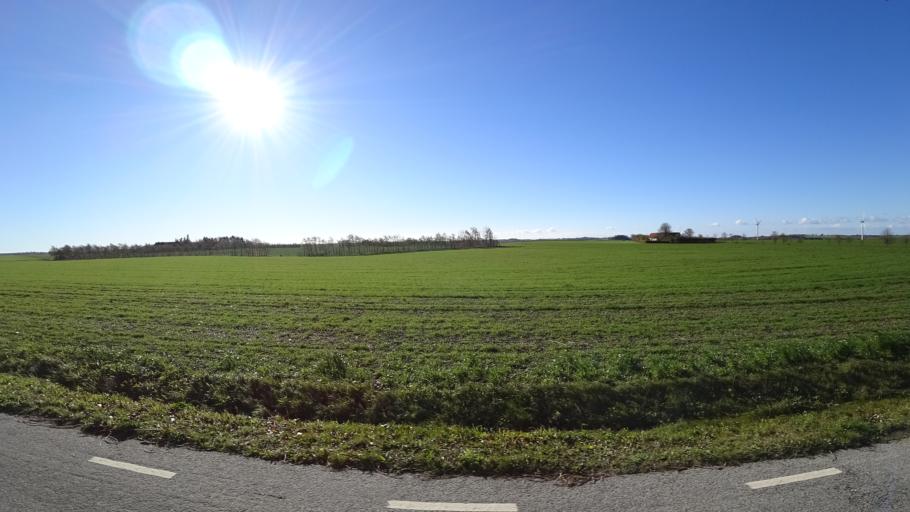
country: SE
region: Skane
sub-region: Svedala Kommun
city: Klagerup
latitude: 55.6166
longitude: 13.2961
